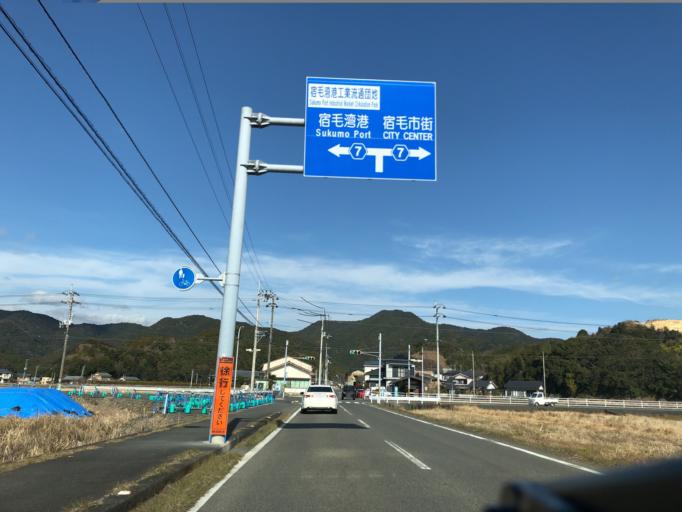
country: JP
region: Kochi
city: Sukumo
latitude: 32.9298
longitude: 132.6962
